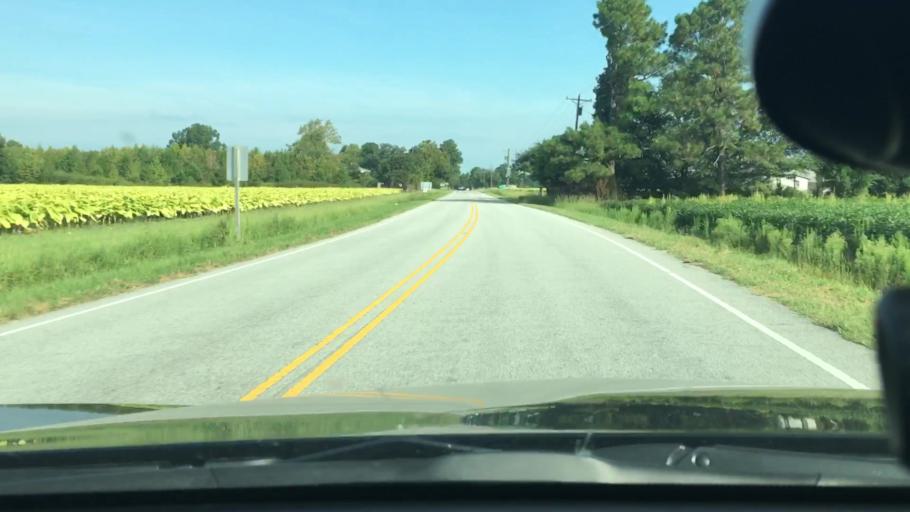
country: US
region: North Carolina
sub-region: Edgecombe County
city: Pinetops
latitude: 35.7464
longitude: -77.5412
